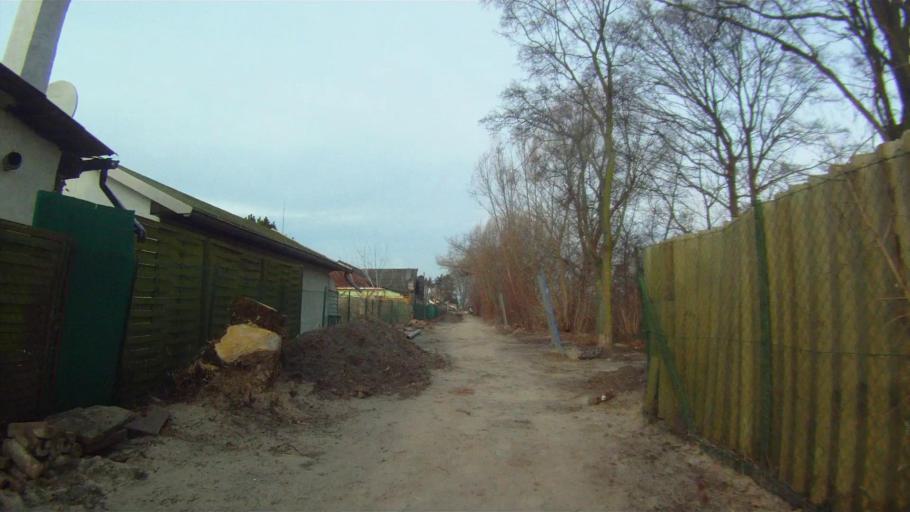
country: DE
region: Berlin
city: Buckow
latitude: 52.4429
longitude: 13.4769
